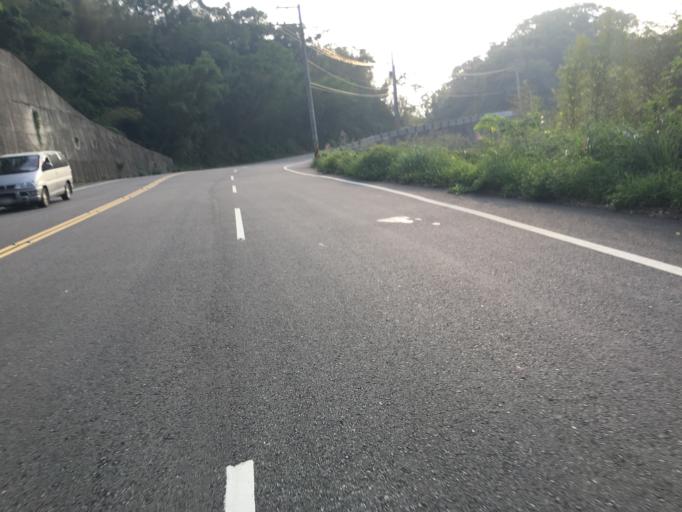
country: TW
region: Taiwan
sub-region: Hsinchu
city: Hsinchu
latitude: 24.7266
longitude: 121.0346
